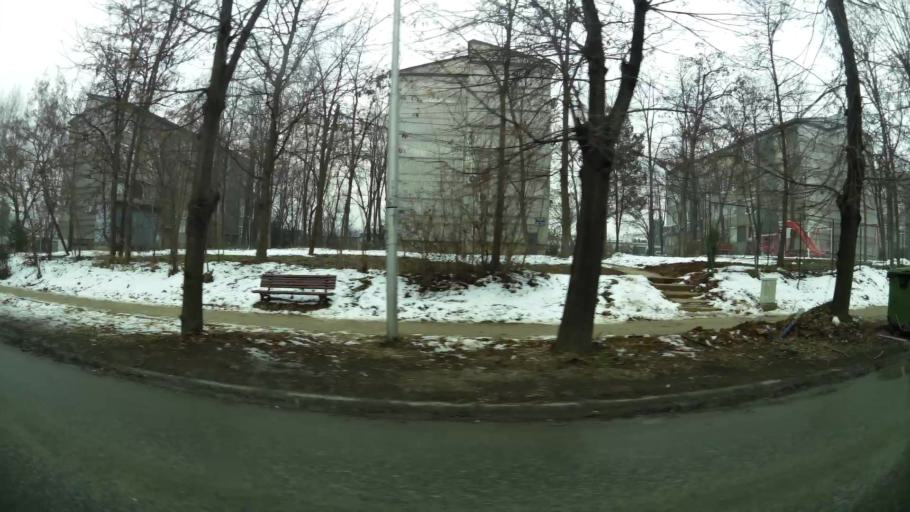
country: MK
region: Cair
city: Cair
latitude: 42.0128
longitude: 21.4580
